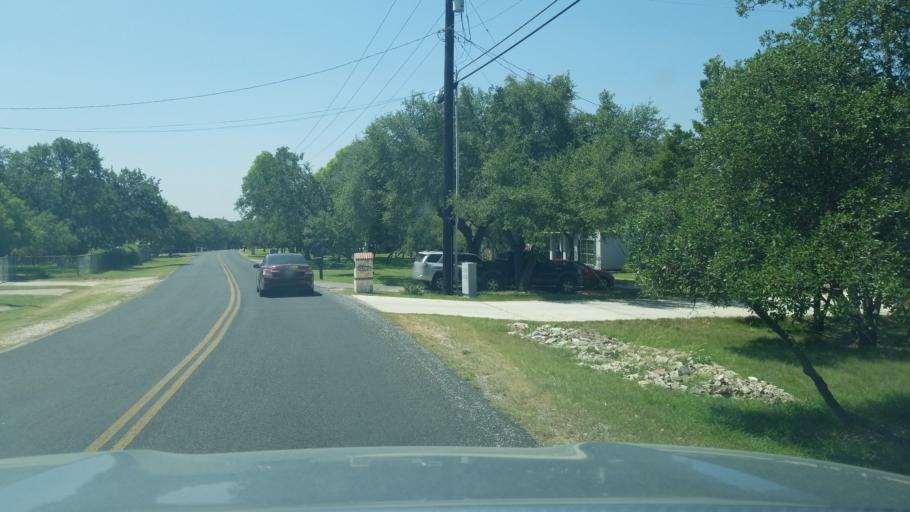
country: US
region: Texas
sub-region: Bexar County
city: Timberwood Park
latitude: 29.7017
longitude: -98.4898
